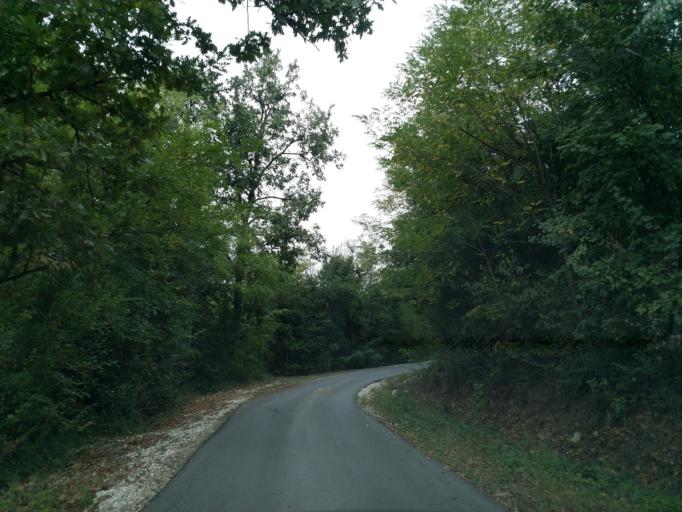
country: RS
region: Central Serbia
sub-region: Sumadijski Okrug
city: Arangelovac
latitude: 44.3134
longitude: 20.5913
